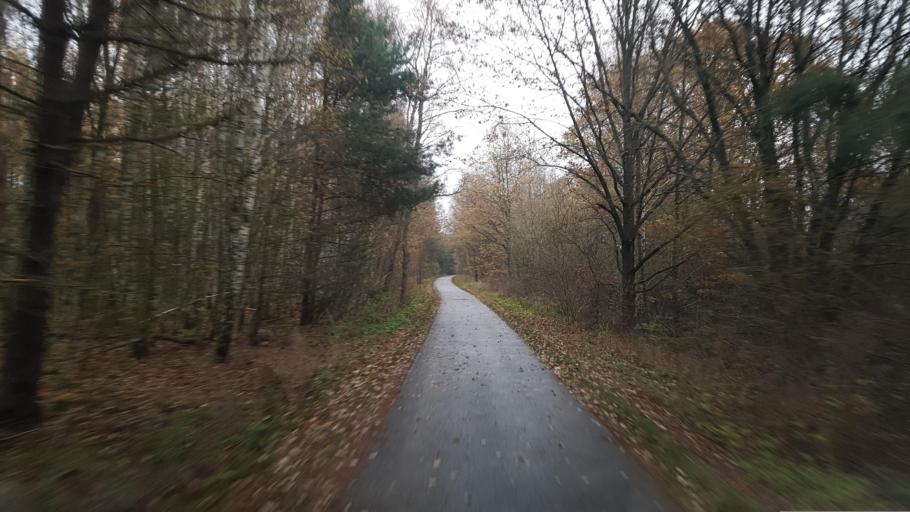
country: DE
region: Brandenburg
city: Crinitz
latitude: 51.7551
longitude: 13.7863
